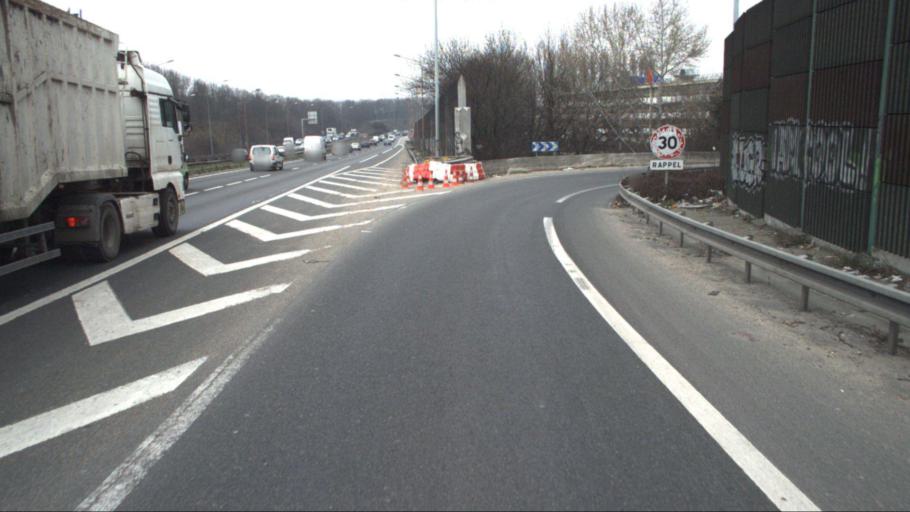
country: FR
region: Ile-de-France
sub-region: Departement du Val-d'Oise
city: Bezons
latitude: 48.9192
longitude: 2.2241
